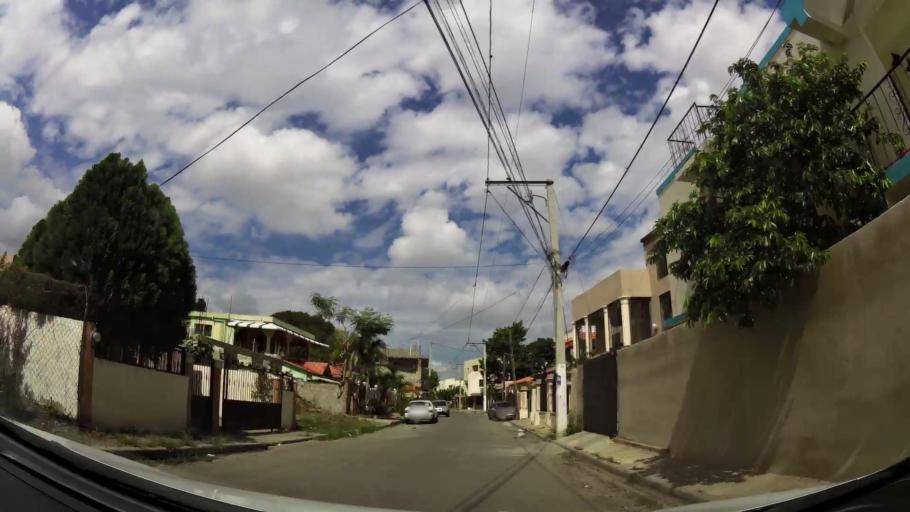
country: DO
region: Santiago
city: Santiago de los Caballeros
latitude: 19.4711
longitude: -70.7006
